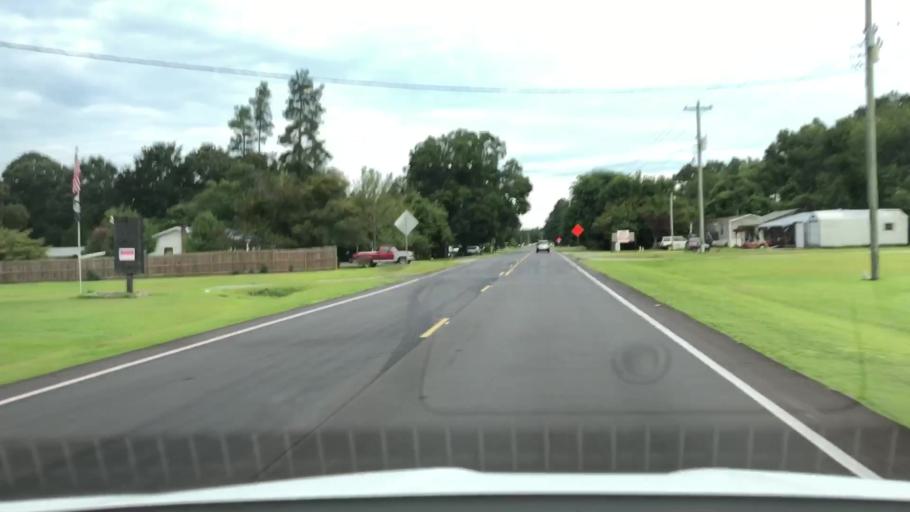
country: US
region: North Carolina
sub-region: Jones County
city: Maysville
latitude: 34.8788
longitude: -77.2045
